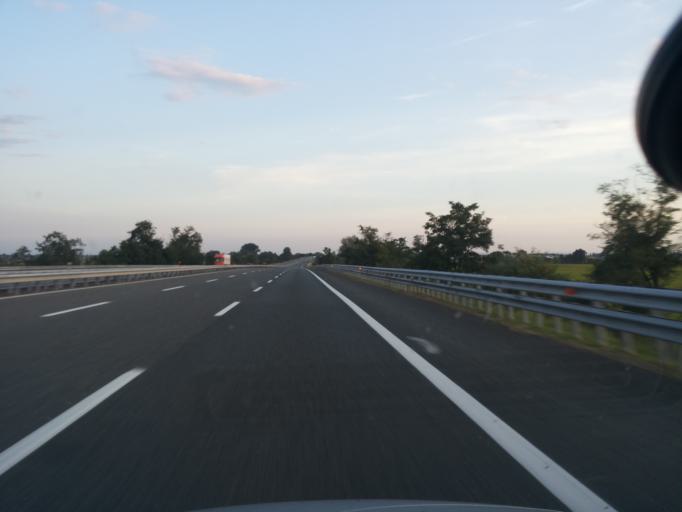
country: IT
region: Piedmont
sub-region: Provincia di Novara
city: Casalvolone
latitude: 45.3813
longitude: 8.4852
